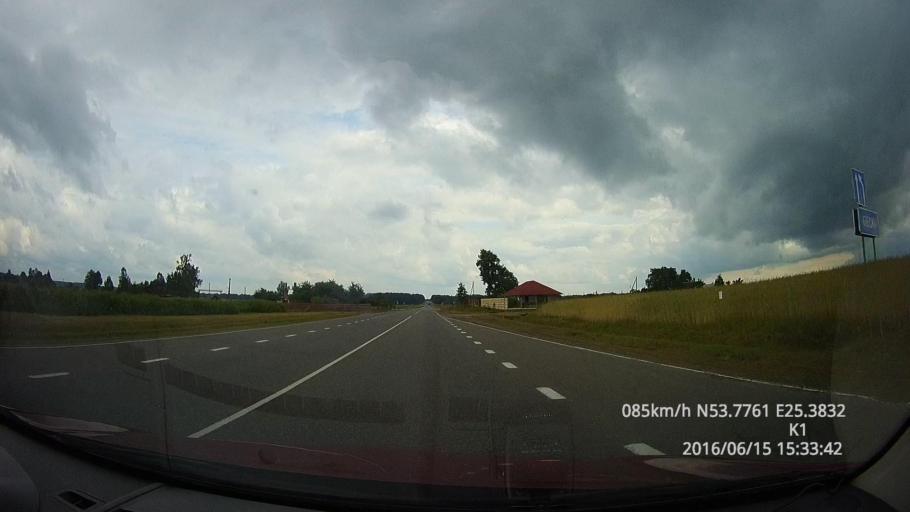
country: BY
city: Berezovka
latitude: 53.7754
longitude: 25.3836
